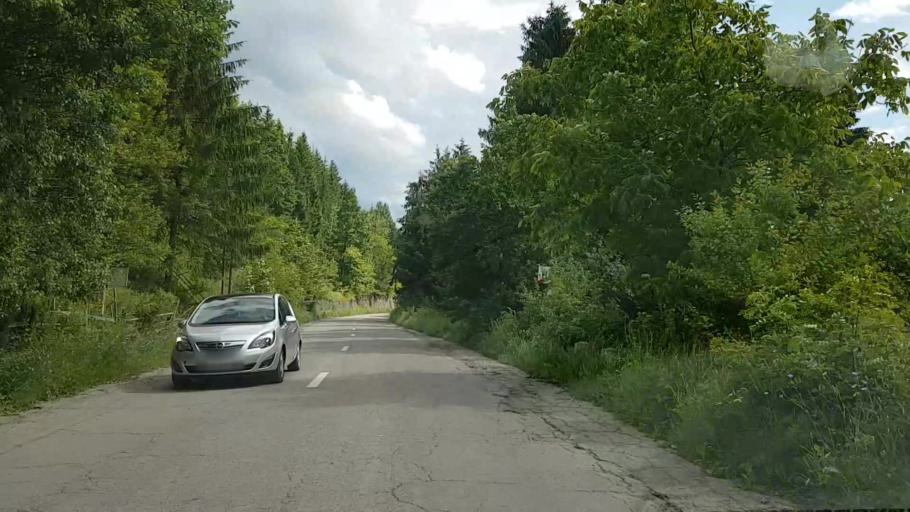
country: RO
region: Neamt
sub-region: Comuna Hangu
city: Hangu
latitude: 47.0553
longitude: 26.0377
